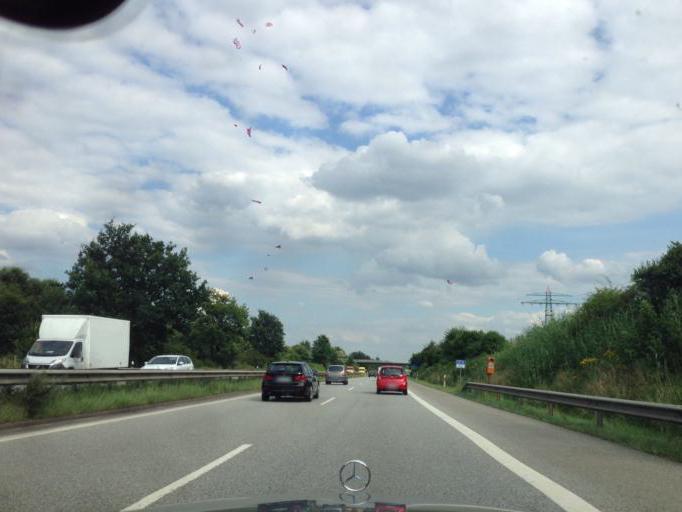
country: DE
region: Schleswig-Holstein
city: Oststeinbek
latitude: 53.4838
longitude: 10.1359
